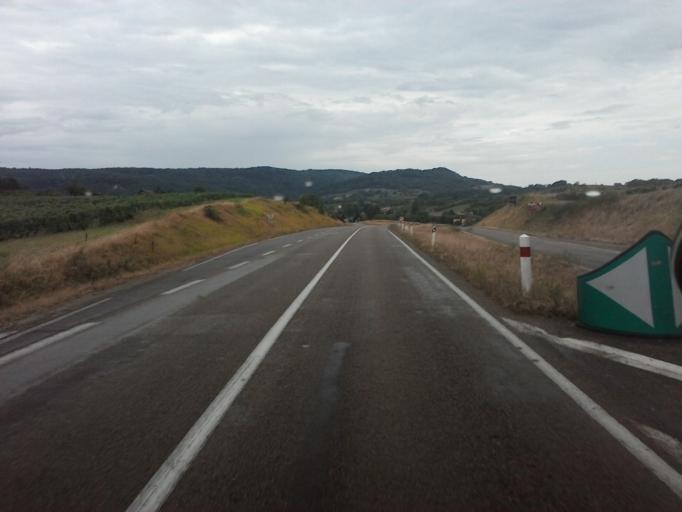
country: FR
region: Franche-Comte
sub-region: Departement du Jura
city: Arbois
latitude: 46.9161
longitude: 5.7713
